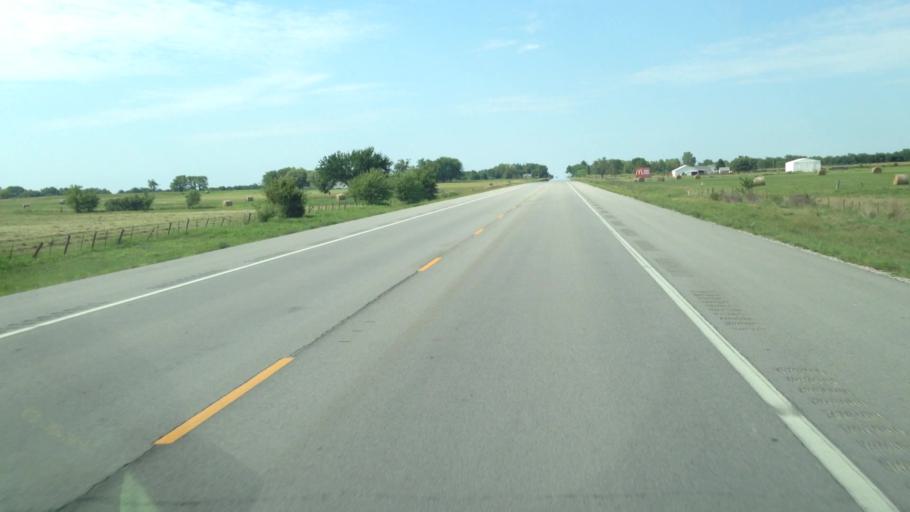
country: US
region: Kansas
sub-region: Labette County
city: Altamont
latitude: 37.2467
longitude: -95.2670
